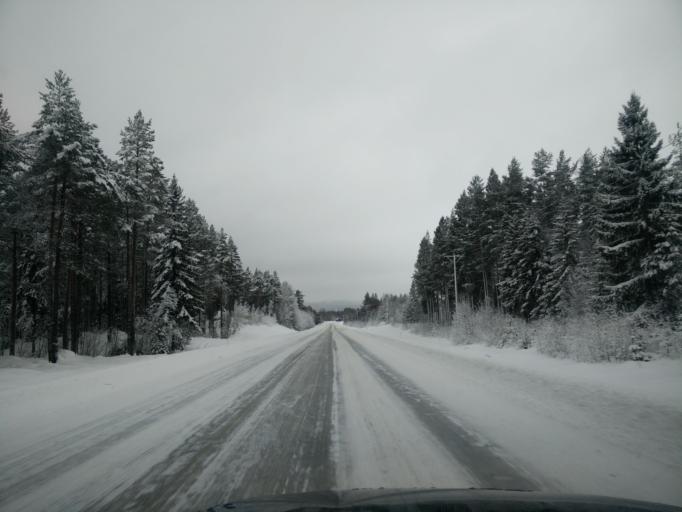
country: SE
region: Vaesternorrland
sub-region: Ange Kommun
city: Ange
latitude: 62.3989
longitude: 15.4552
